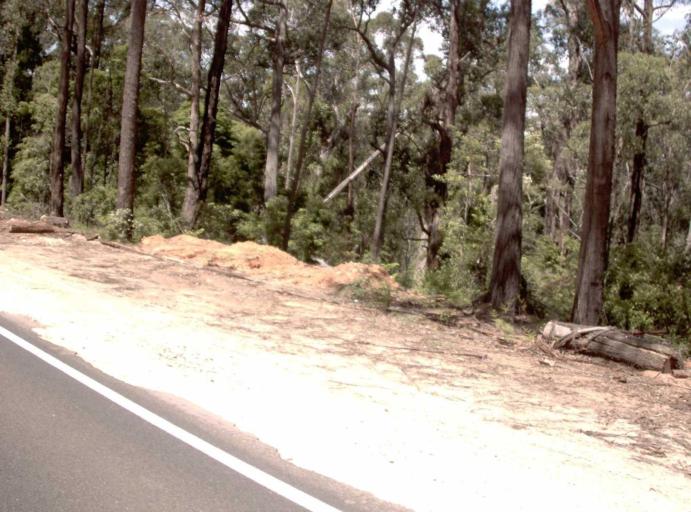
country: AU
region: New South Wales
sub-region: Bombala
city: Bombala
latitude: -37.5813
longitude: 149.0095
